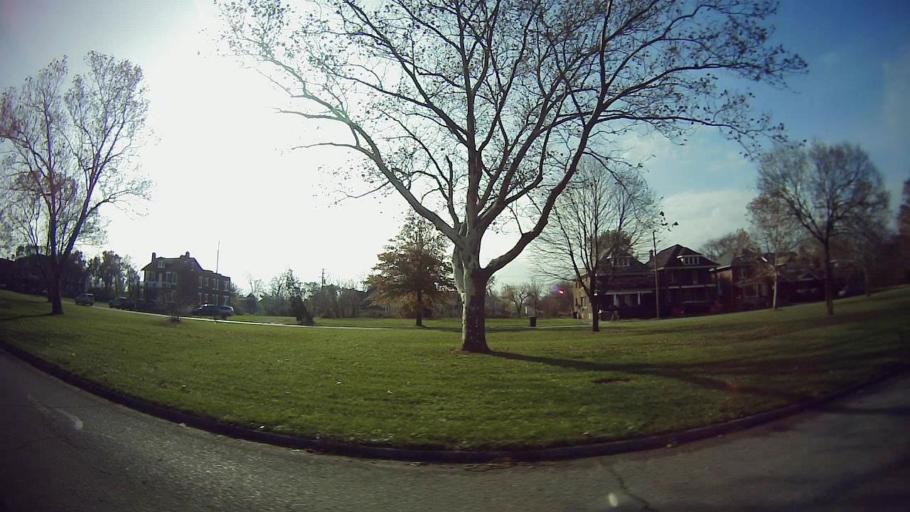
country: US
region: Michigan
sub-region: Wayne County
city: Detroit
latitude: 42.3438
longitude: -83.1068
